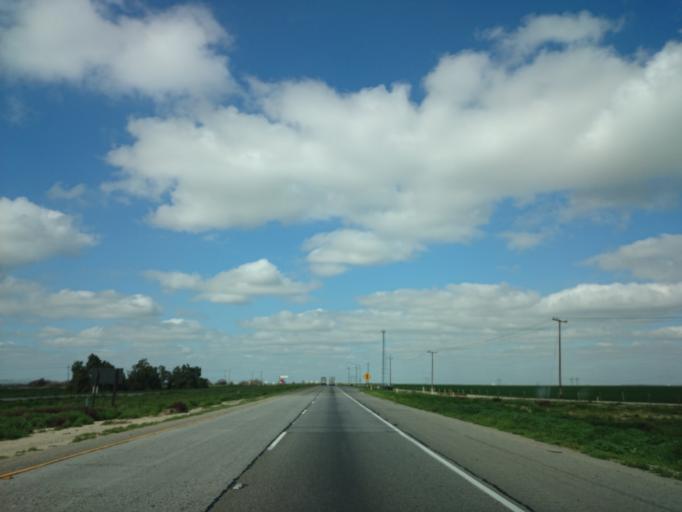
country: US
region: California
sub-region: Kern County
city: Greenfield
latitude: 35.2093
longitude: -119.1628
